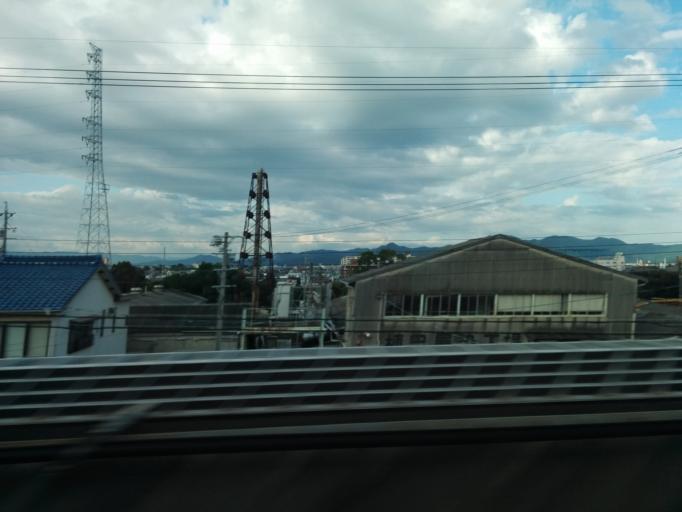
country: JP
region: Aichi
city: Toyohashi
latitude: 34.7441
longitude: 137.3963
